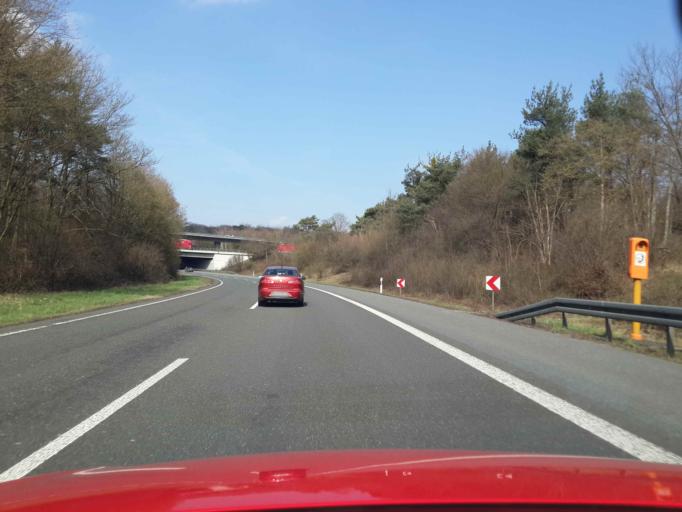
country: DE
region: Hesse
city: Raunheim
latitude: 50.0249
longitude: 8.4952
